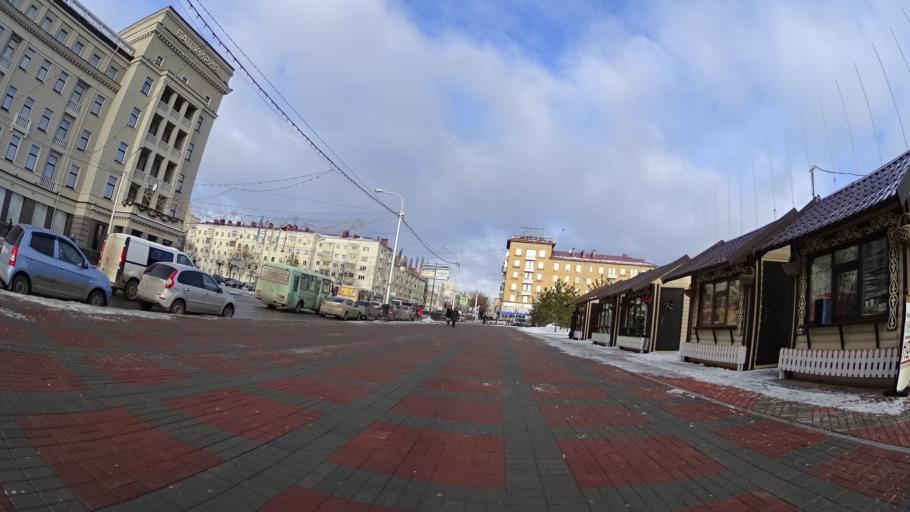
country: RU
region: Bashkortostan
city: Ufa
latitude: 54.7302
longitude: 55.9497
